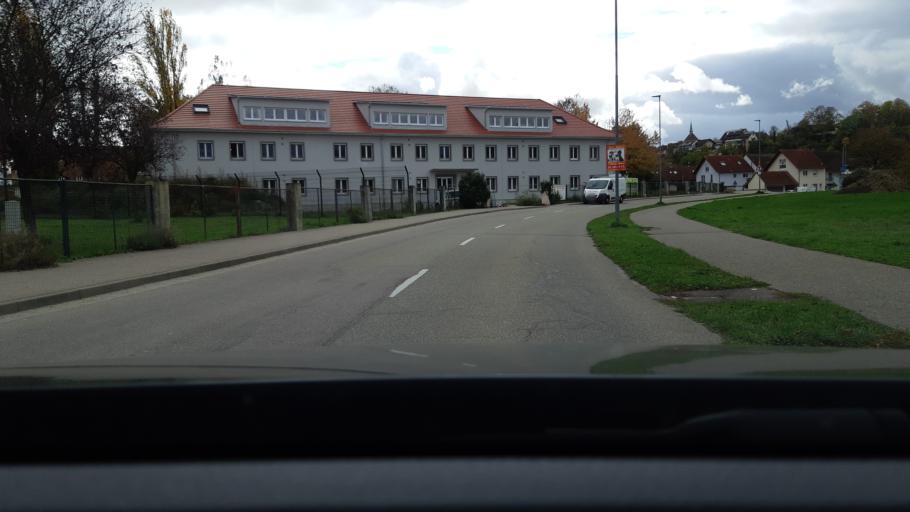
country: DE
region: Baden-Wuerttemberg
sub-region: Freiburg Region
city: Breisach am Rhein
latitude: 48.0370
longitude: 7.5807
